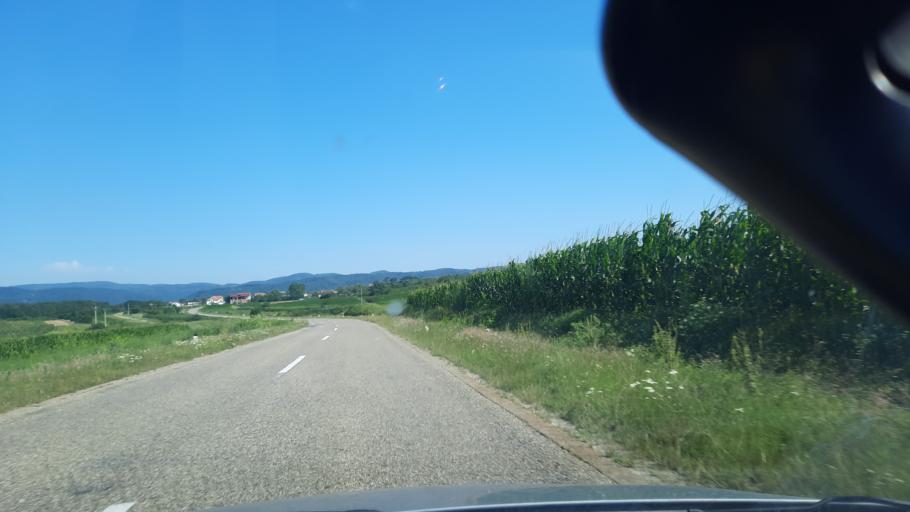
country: RS
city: Turija
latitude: 44.5588
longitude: 21.5374
